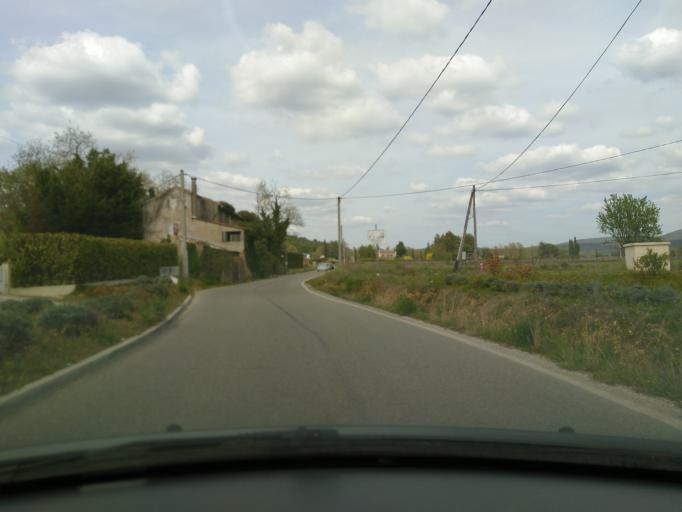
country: FR
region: Rhone-Alpes
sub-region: Departement de l'Ardeche
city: Ruoms
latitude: 44.4184
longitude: 4.4121
